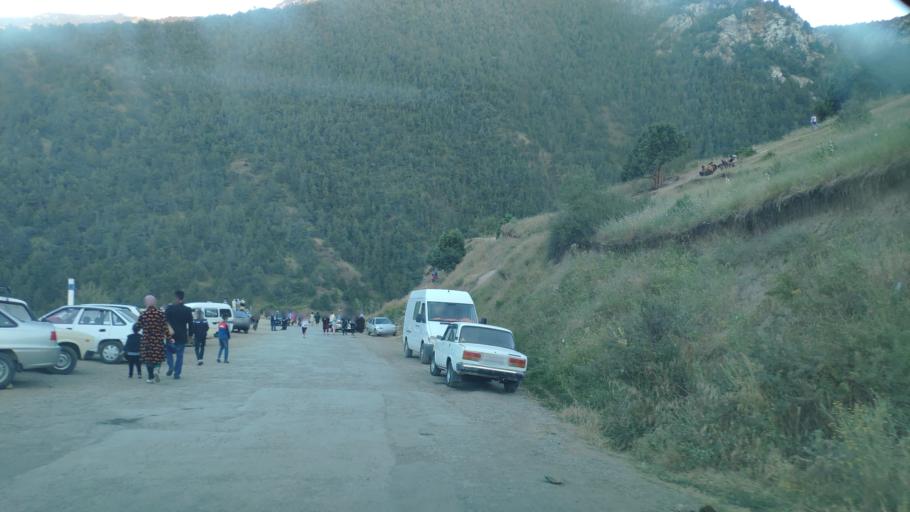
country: TJ
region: Viloyati Sughd
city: Ayni
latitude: 39.6325
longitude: 68.4916
